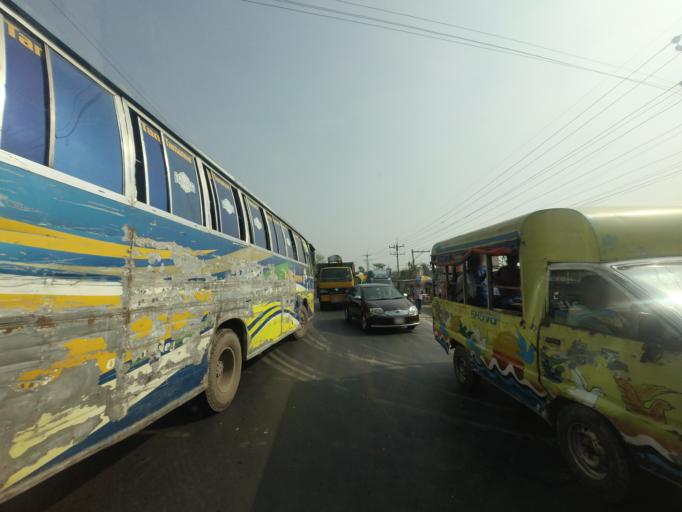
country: BD
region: Dhaka
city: Narsingdi
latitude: 23.8469
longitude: 90.6292
